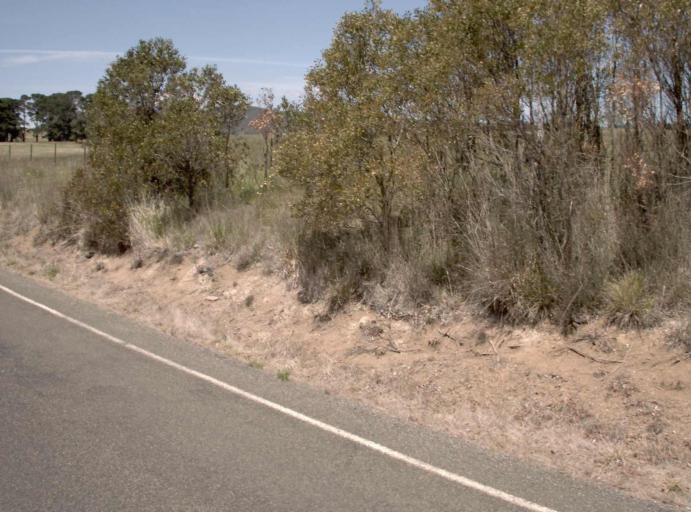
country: AU
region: Victoria
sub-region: Alpine
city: Mount Beauty
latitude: -37.1457
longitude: 147.6478
